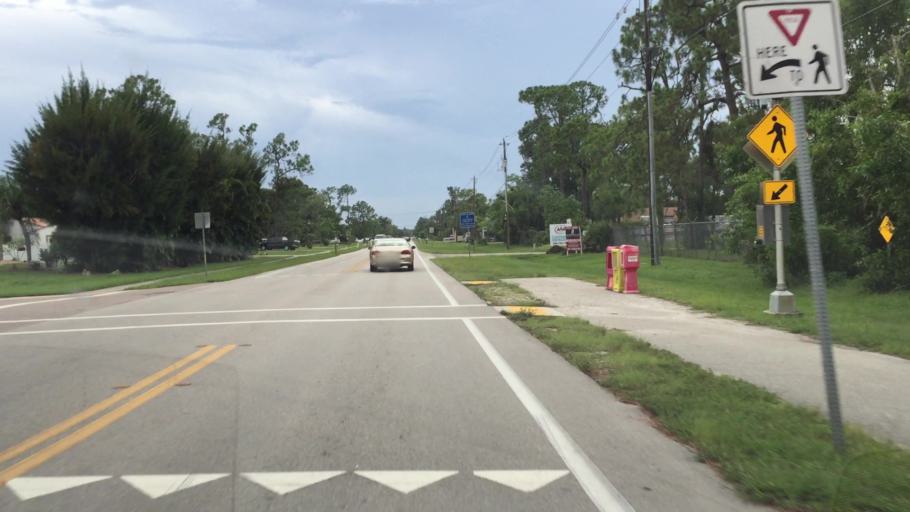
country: US
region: Florida
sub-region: Lee County
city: Villas
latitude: 26.5646
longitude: -81.8561
